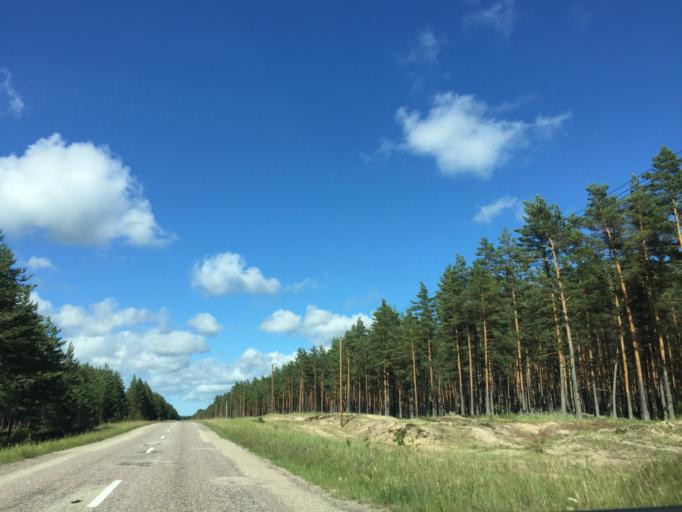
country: LV
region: Ventspils
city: Ventspils
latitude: 57.5207
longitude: 21.7008
